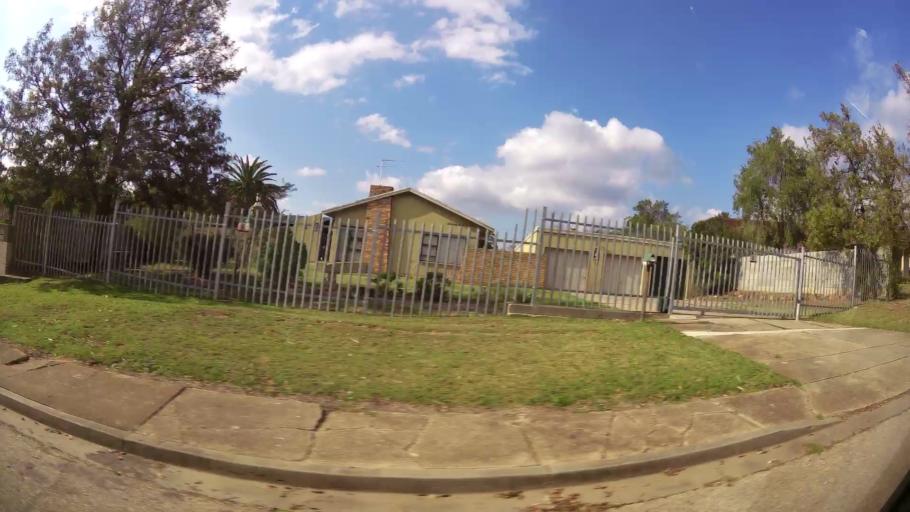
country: ZA
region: Eastern Cape
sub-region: Nelson Mandela Bay Metropolitan Municipality
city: Uitenhage
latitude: -33.7321
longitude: 25.4066
